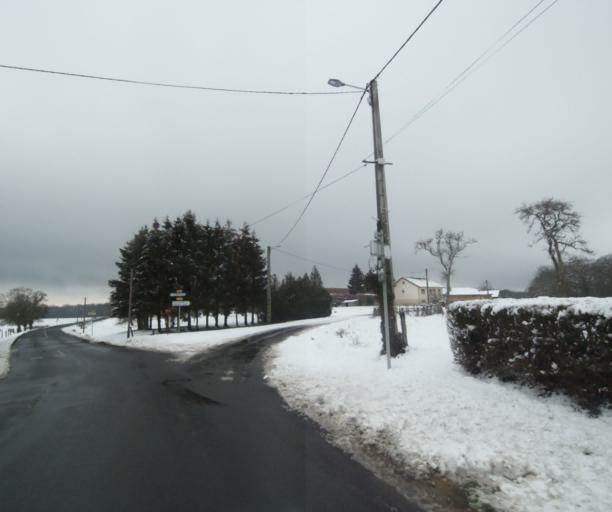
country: FR
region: Champagne-Ardenne
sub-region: Departement de la Haute-Marne
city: Laneuville-a-Remy
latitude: 48.4643
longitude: 4.9092
